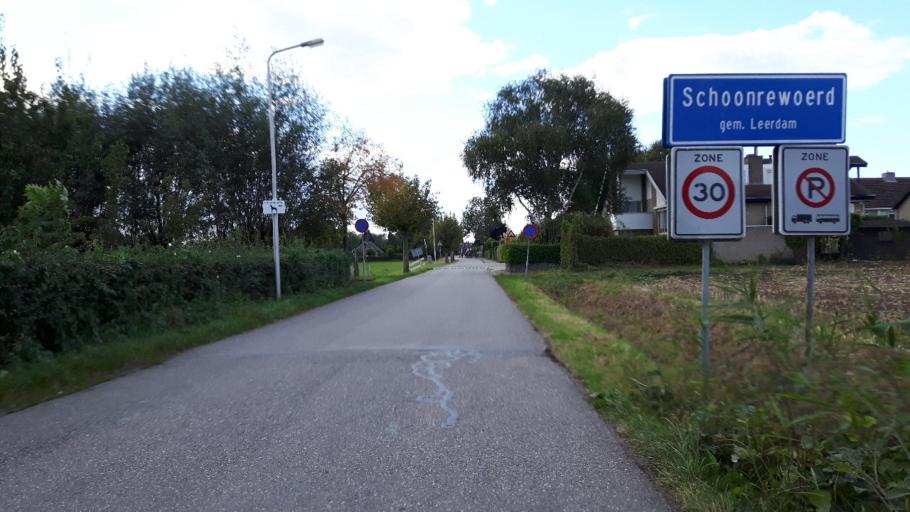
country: NL
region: South Holland
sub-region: Gemeente Leerdam
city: Leerdam
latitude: 51.9183
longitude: 5.1206
